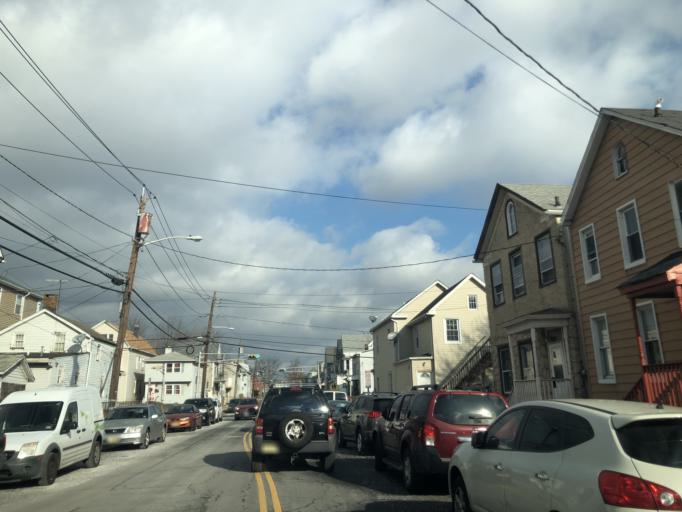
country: US
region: New Jersey
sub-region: Union County
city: Elizabeth
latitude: 40.6678
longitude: -74.2062
